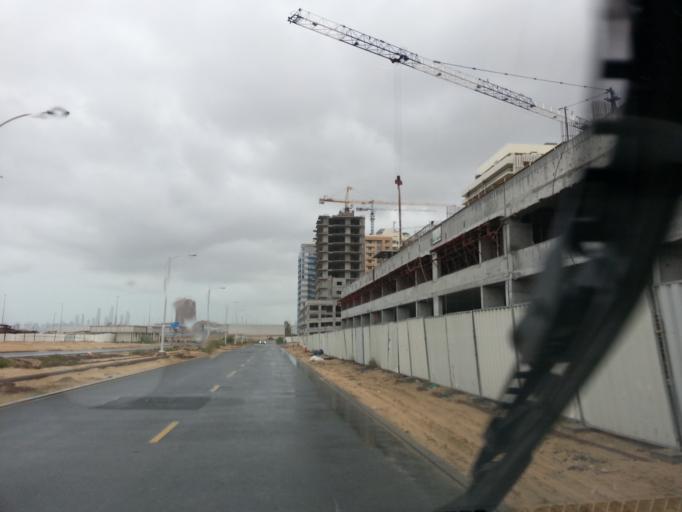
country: AE
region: Dubai
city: Dubai
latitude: 25.0357
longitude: 55.2060
